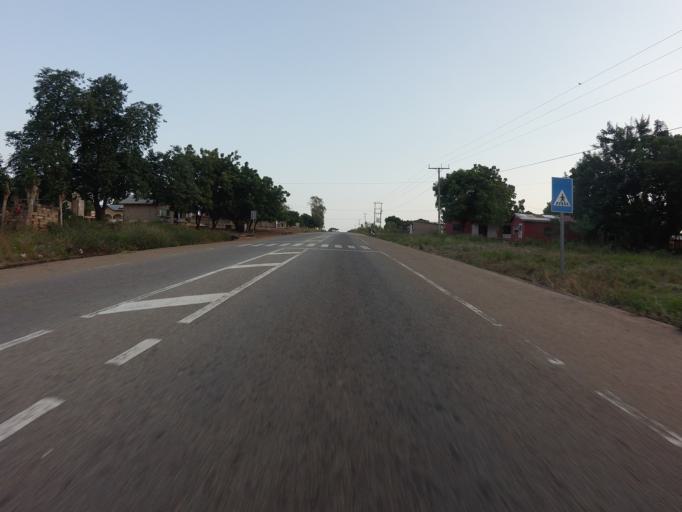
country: GH
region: Volta
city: Anloga
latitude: 6.0513
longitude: 0.6046
